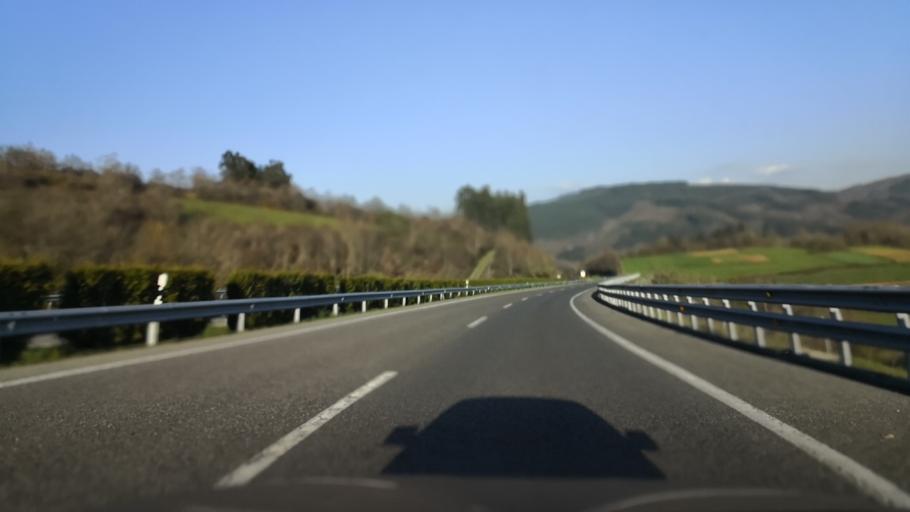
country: ES
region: Galicia
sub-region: Provincia de Lugo
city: Baralla
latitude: 42.9003
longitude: -7.2660
